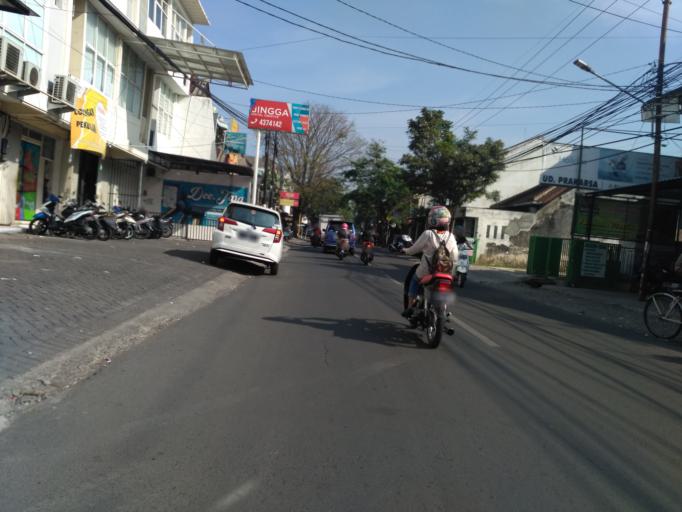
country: ID
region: East Java
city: Malang
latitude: -7.9466
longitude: 112.6228
